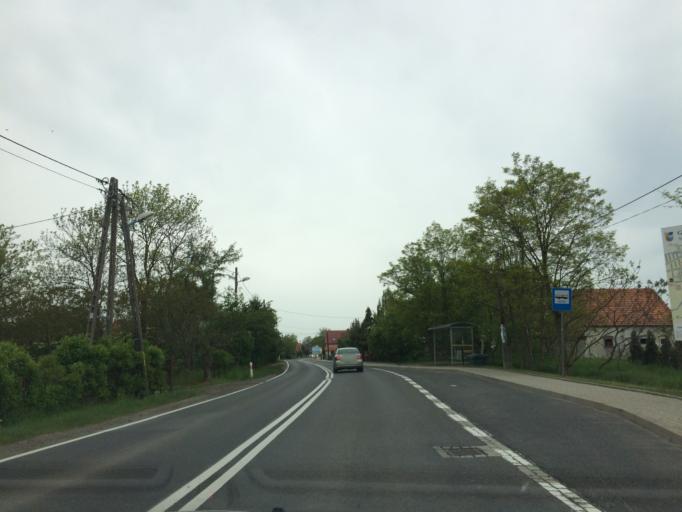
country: PL
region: Lower Silesian Voivodeship
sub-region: Powiat legnicki
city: Kunice
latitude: 51.2468
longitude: 16.2951
